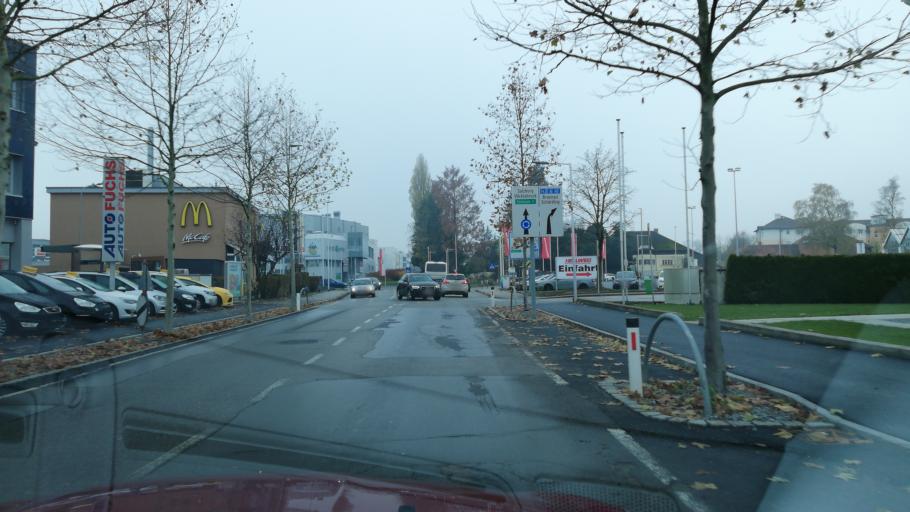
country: AT
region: Upper Austria
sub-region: Politischer Bezirk Ried im Innkreis
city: Ried im Innkreis
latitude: 48.2130
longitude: 13.4838
